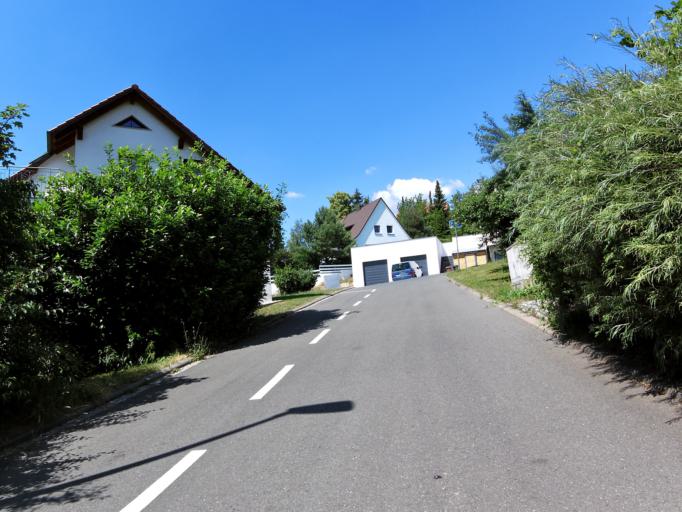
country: DE
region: Bavaria
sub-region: Regierungsbezirk Unterfranken
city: Gadheim
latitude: 49.8217
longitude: 9.9223
